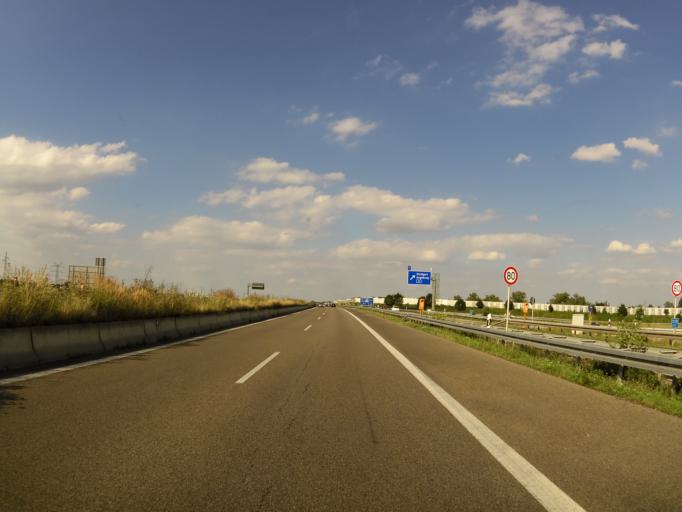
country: DE
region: Bavaria
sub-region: Upper Bavaria
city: Pasing
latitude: 48.1799
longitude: 11.4316
